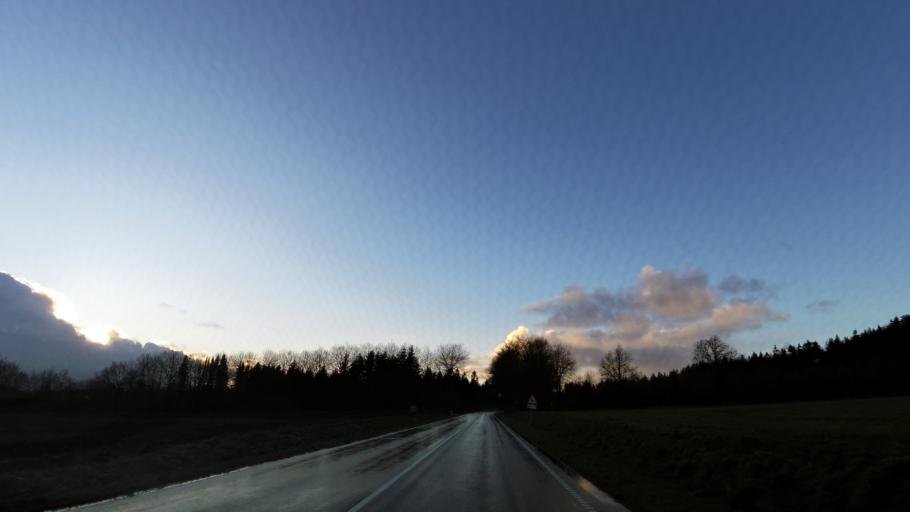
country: DK
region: Central Jutland
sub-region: Ikast-Brande Kommune
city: Brande
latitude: 56.0087
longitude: 9.0826
